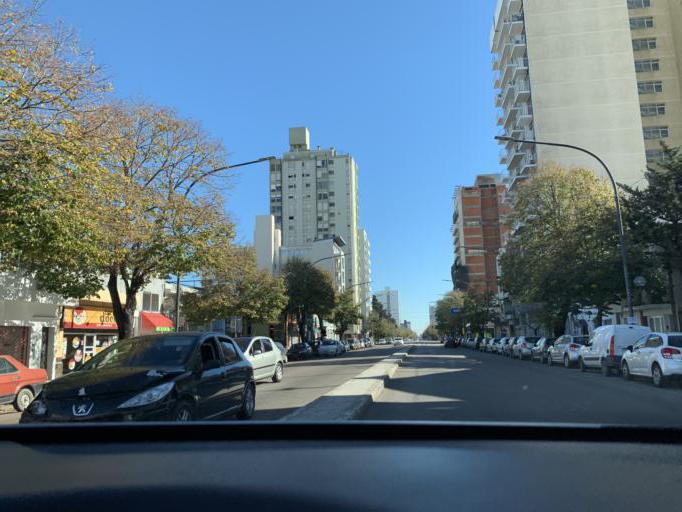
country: AR
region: Buenos Aires
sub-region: Partido de La Plata
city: La Plata
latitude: -34.9073
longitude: -57.9599
